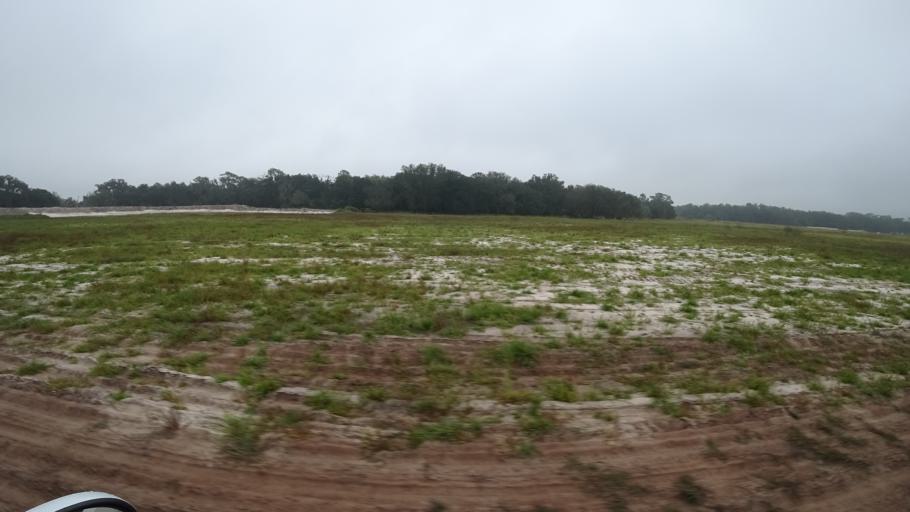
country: US
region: Florida
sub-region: Sarasota County
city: Lake Sarasota
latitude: 27.2937
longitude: -82.2158
